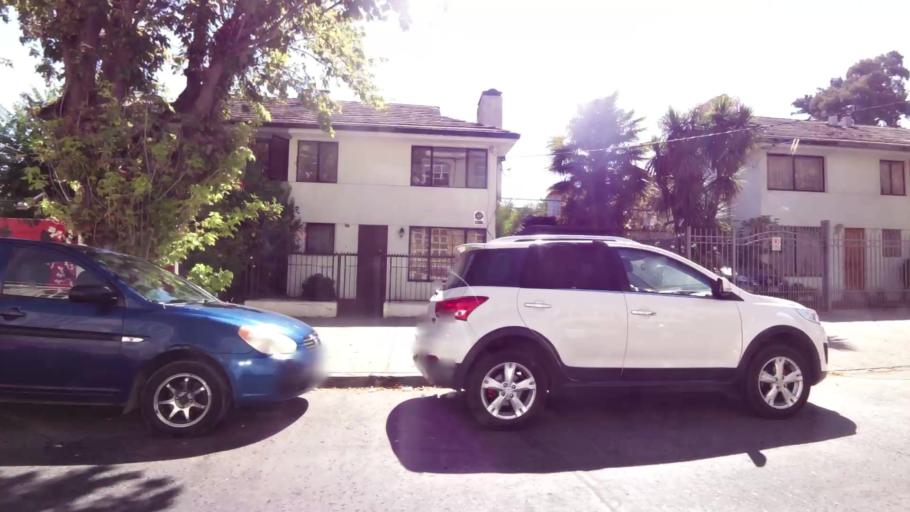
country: CL
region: Maule
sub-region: Provincia de Talca
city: Talca
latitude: -35.4231
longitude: -71.6581
